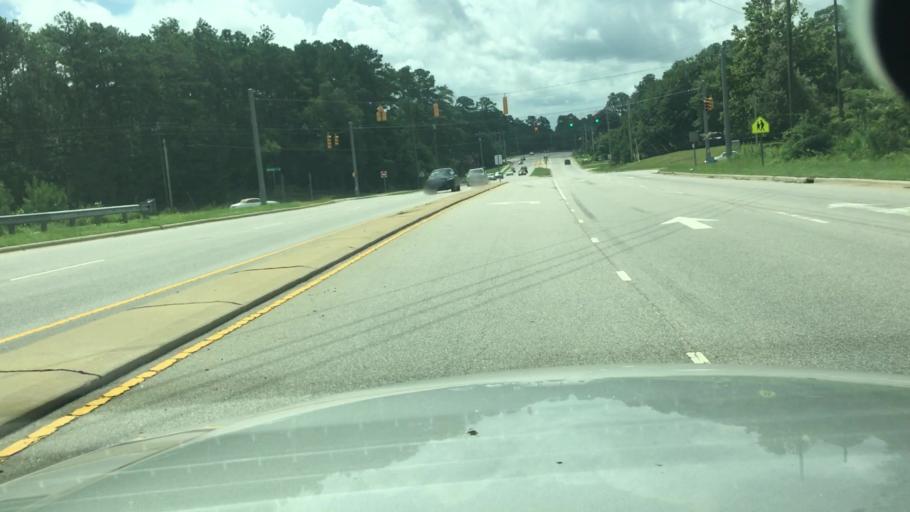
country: US
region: North Carolina
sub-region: Cumberland County
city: Hope Mills
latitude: 35.0353
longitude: -78.9860
